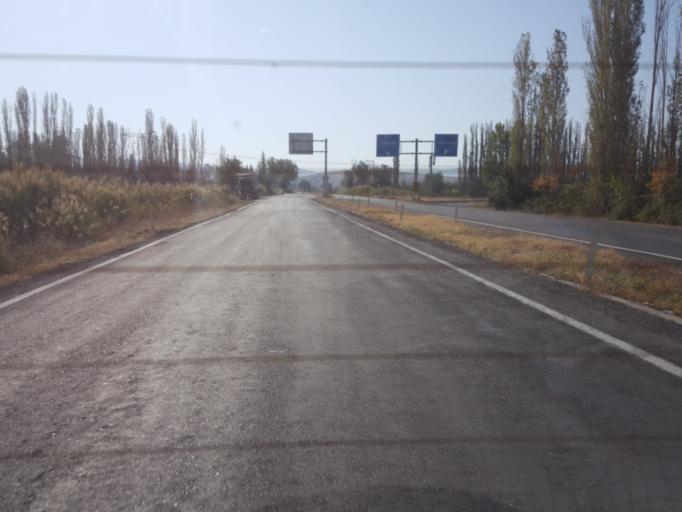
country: TR
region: Corum
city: Seydim
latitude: 40.5960
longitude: 34.5923
